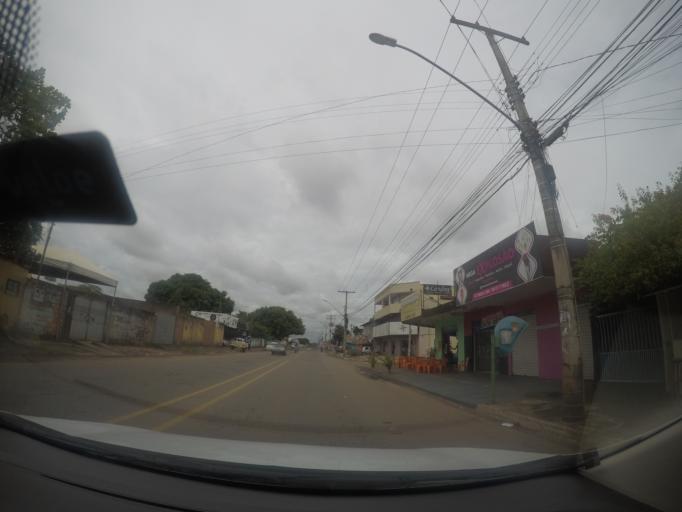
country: BR
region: Goias
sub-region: Goiania
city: Goiania
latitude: -16.6886
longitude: -49.3354
